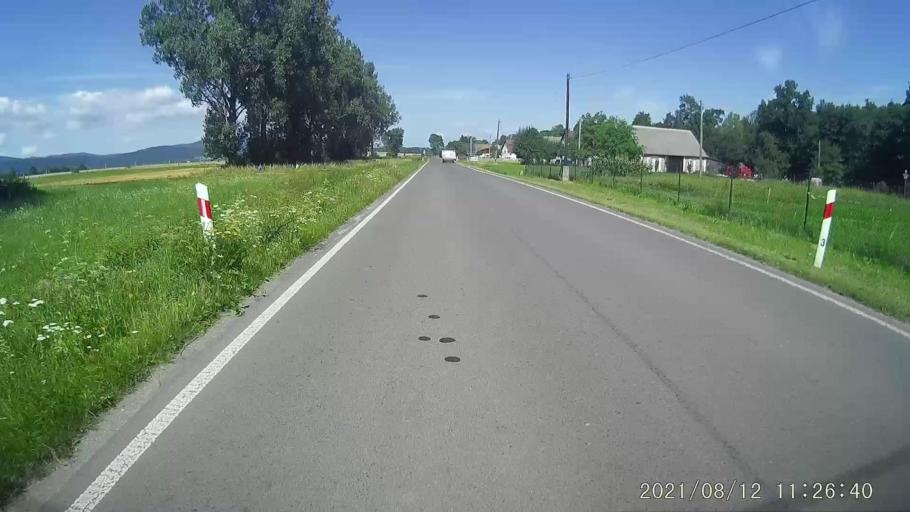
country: PL
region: Lower Silesian Voivodeship
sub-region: Powiat klodzki
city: Bystrzyca Klodzka
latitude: 50.2747
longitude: 16.6876
